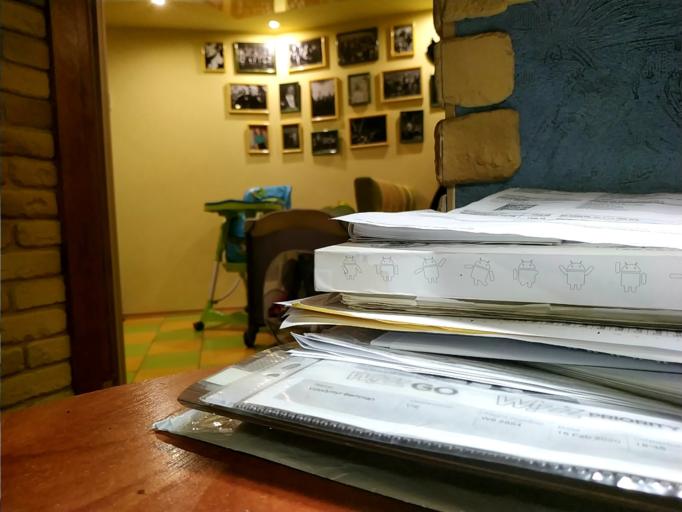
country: RU
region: Arkhangelskaya
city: Kargopol'
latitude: 61.3084
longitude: 39.4361
